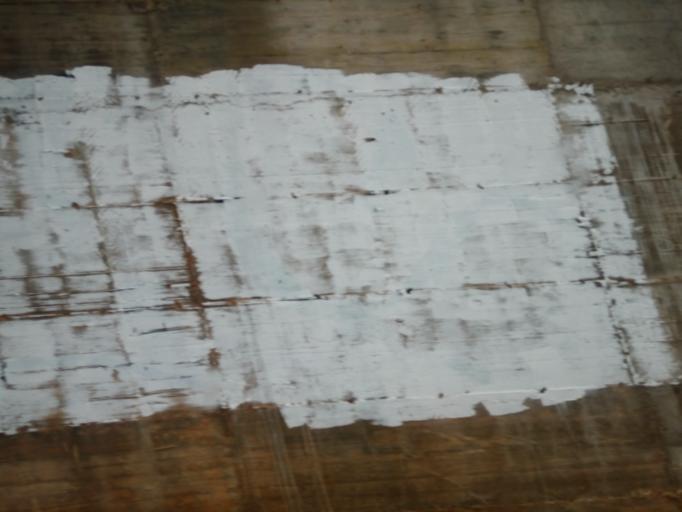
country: PT
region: Faro
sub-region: Loule
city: Loule
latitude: 37.1100
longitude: -8.0052
